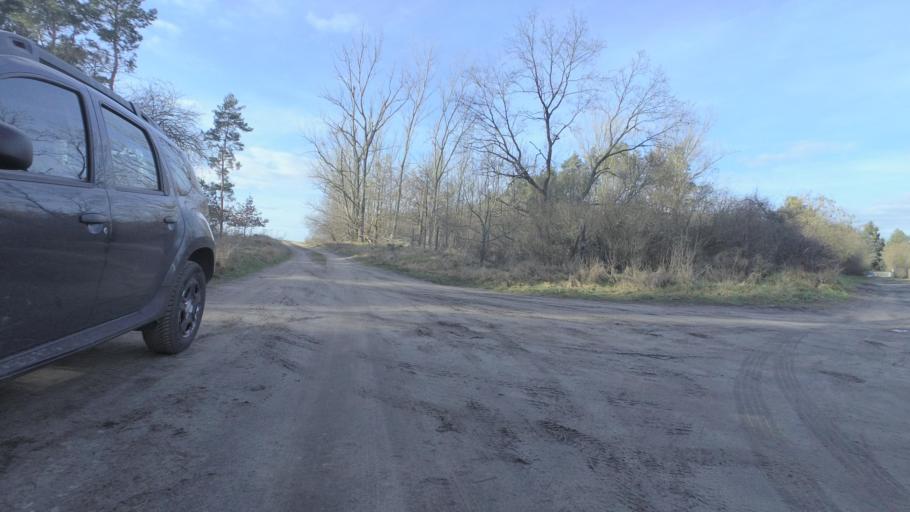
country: DE
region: Brandenburg
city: Trebbin
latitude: 52.2258
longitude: 13.2328
